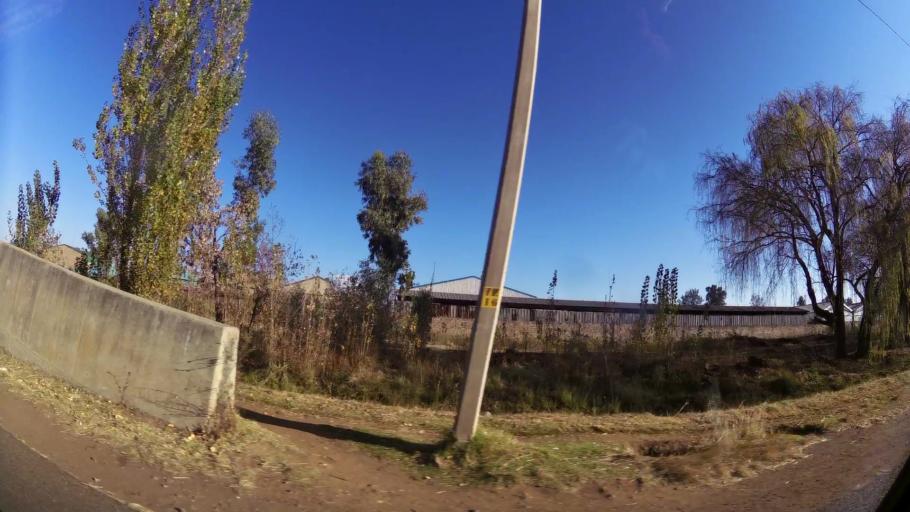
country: ZA
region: Gauteng
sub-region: Ekurhuleni Metropolitan Municipality
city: Germiston
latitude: -26.3488
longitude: 28.1268
